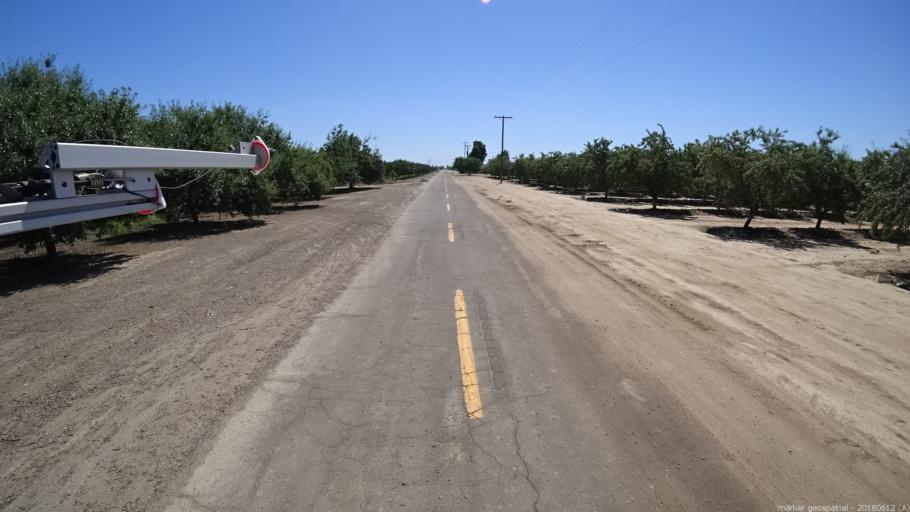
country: US
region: California
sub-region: Madera County
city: Chowchilla
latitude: 37.0254
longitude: -120.3268
